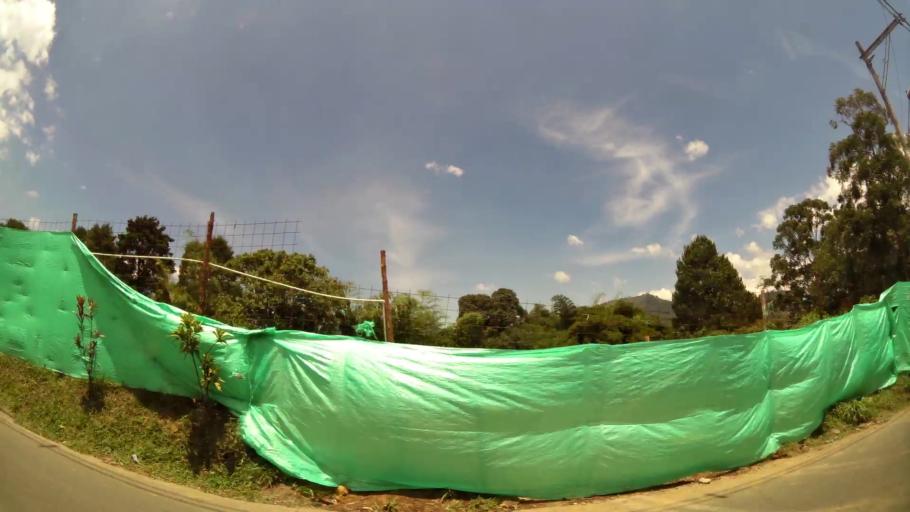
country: CO
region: Antioquia
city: La Estrella
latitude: 6.1640
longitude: -75.6376
